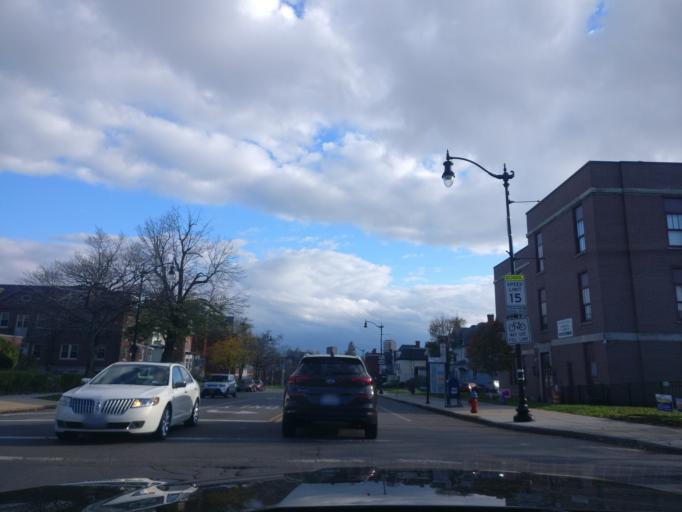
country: US
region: New York
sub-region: Erie County
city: Buffalo
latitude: 42.9013
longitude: -78.8922
